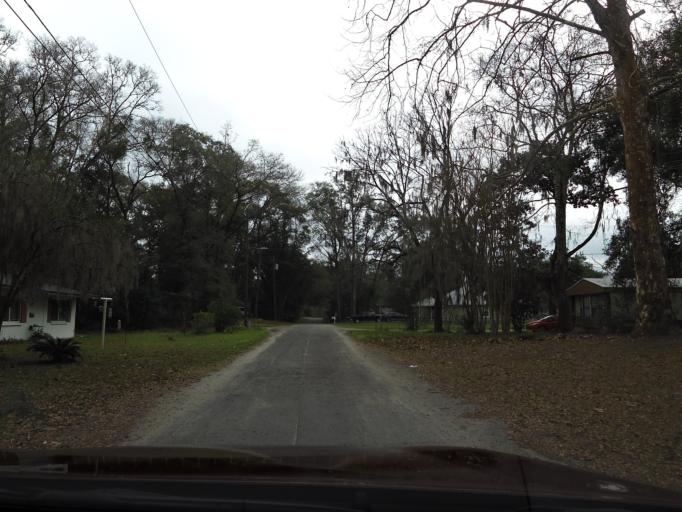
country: US
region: Florida
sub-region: Alachua County
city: High Springs
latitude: 29.8235
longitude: -82.6016
